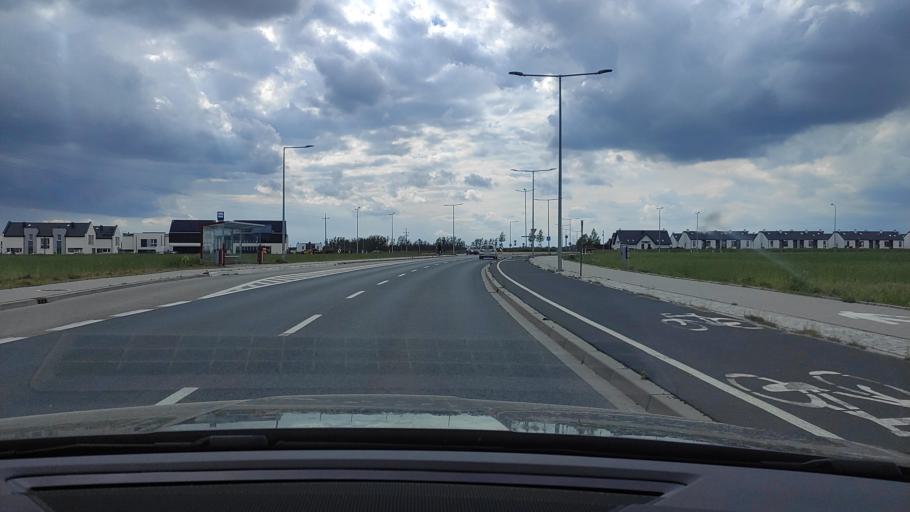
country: PL
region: Greater Poland Voivodeship
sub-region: Powiat poznanski
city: Swarzedz
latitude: 52.3809
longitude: 17.0685
